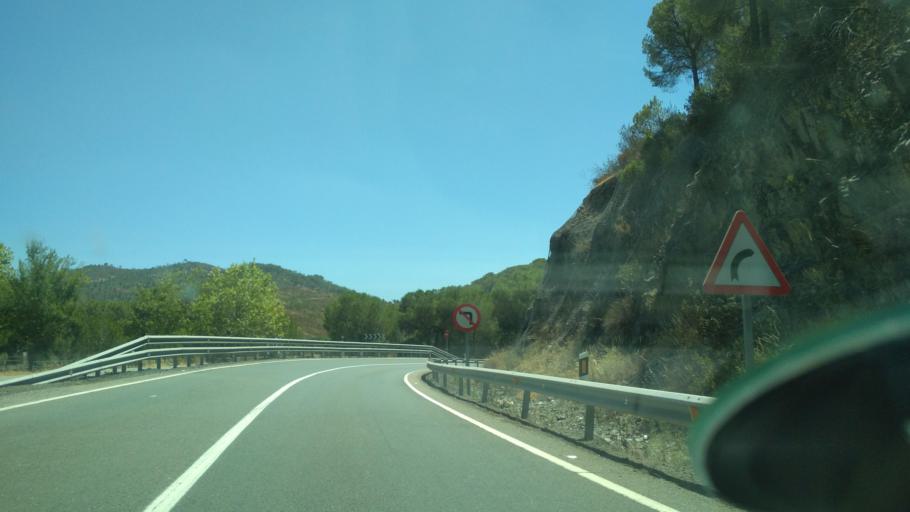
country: ES
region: Andalusia
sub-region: Provincia de Huelva
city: Campofrio
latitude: 37.7479
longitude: -6.5843
